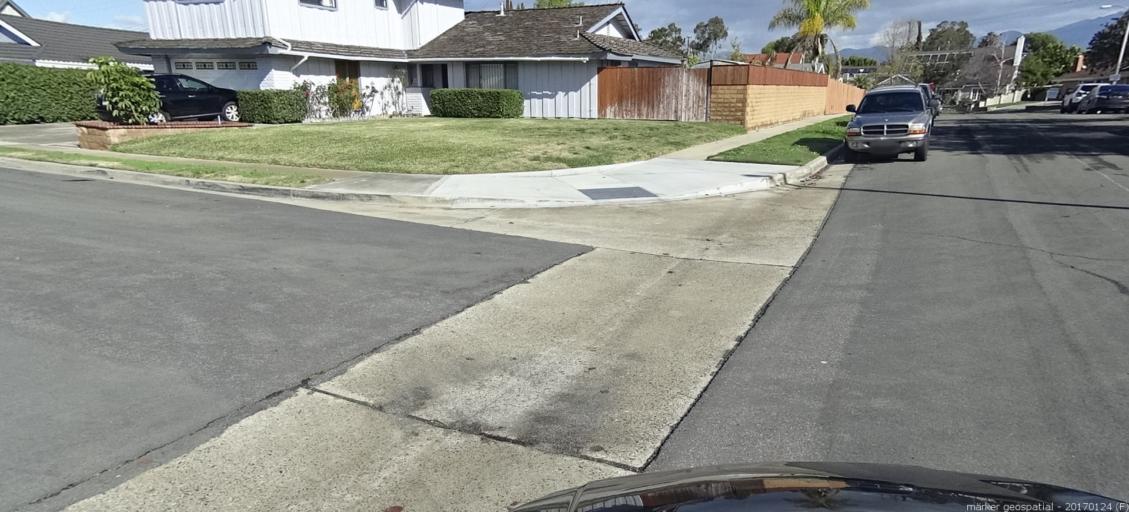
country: US
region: California
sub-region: Orange County
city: Laguna Hills
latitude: 33.6209
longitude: -117.7070
